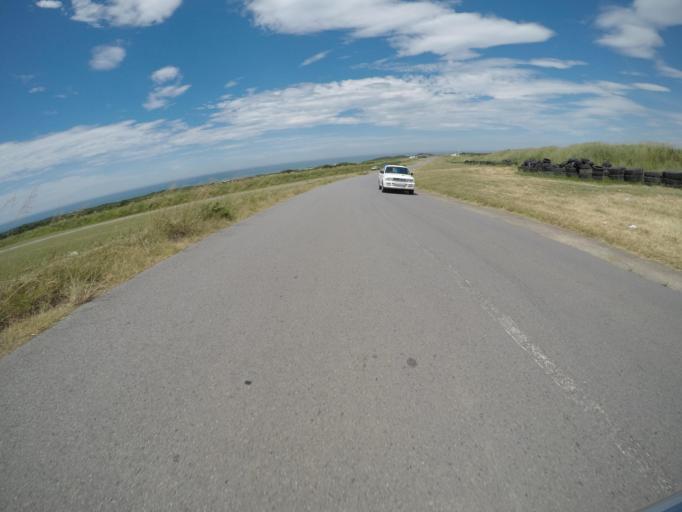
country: ZA
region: Eastern Cape
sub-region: Buffalo City Metropolitan Municipality
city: East London
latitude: -33.0438
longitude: 27.8727
